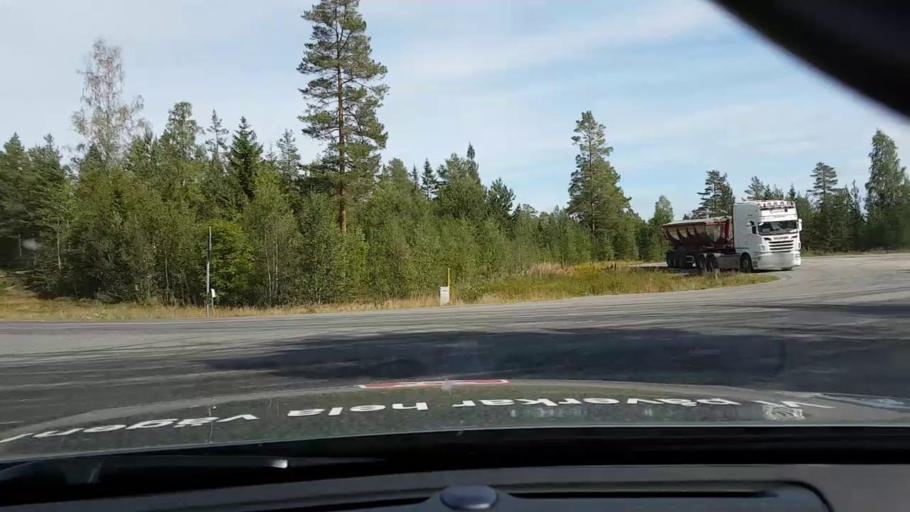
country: SE
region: Vaesternorrland
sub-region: OErnskoeldsviks Kommun
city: Husum
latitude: 63.4806
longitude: 19.2964
